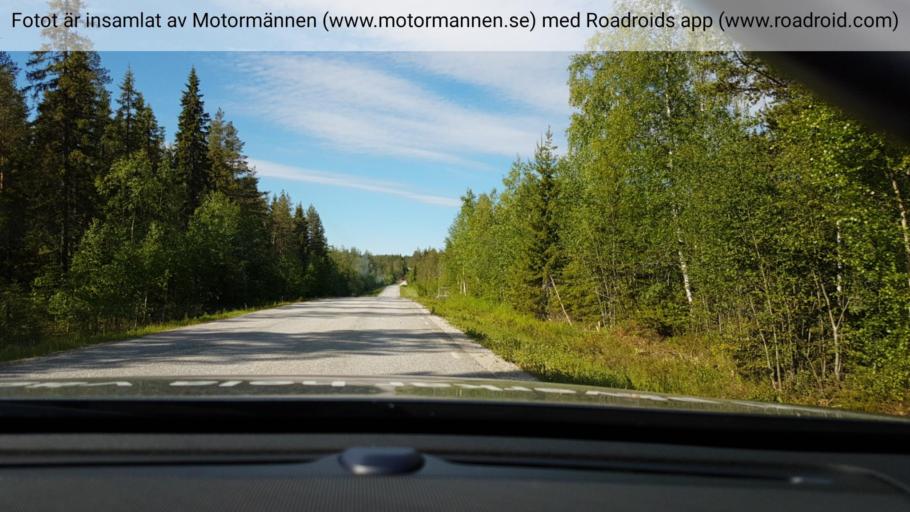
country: SE
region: Vaesterbotten
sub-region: Bjurholms Kommun
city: Bjurholm
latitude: 63.9813
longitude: 19.3318
